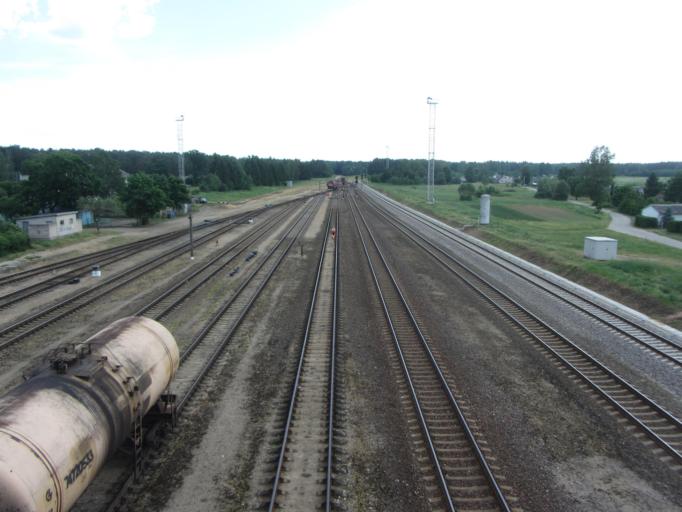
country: LT
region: Kauno apskritis
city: Jonava
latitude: 55.0393
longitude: 24.3277
